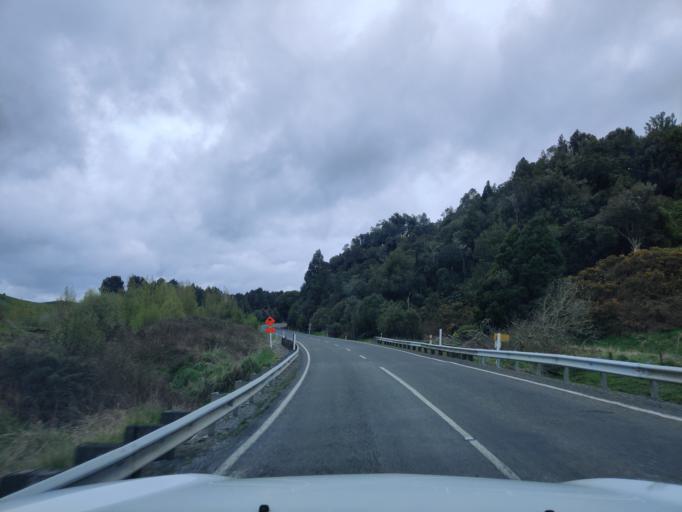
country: NZ
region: Waikato
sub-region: Otorohanga District
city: Otorohanga
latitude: -38.5307
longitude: 175.1775
